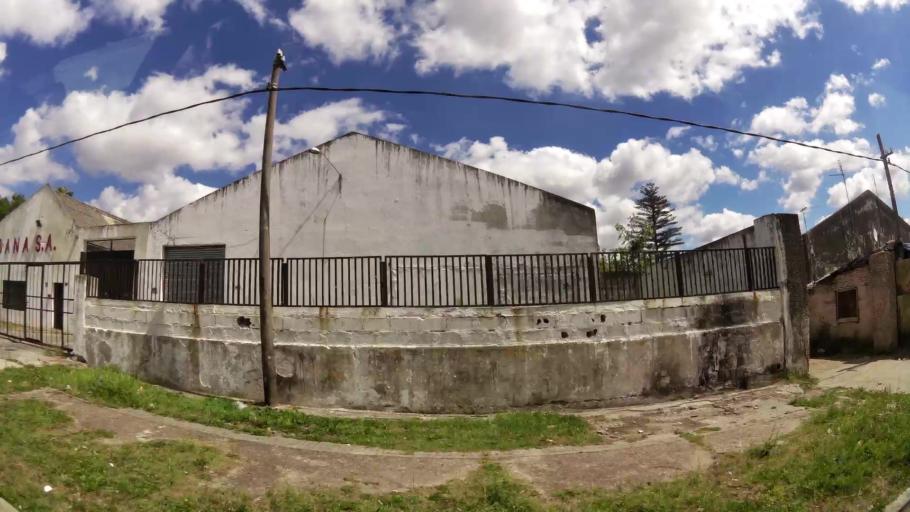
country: UY
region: Canelones
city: Paso de Carrasco
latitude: -34.8331
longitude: -56.1202
